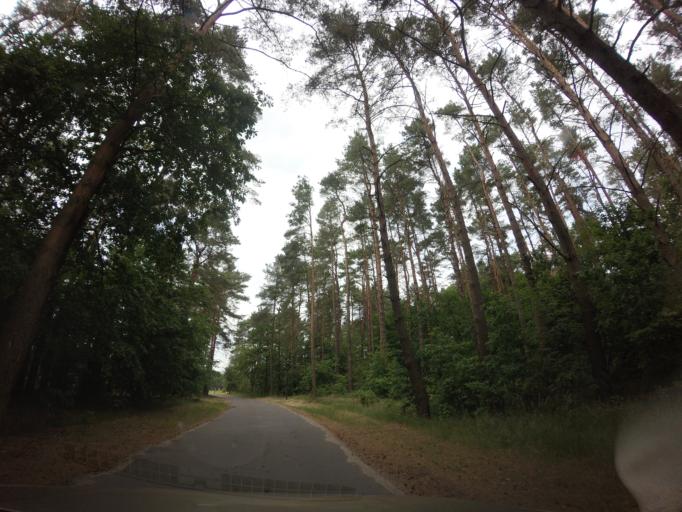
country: PL
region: West Pomeranian Voivodeship
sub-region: Powiat szczecinecki
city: Borne Sulinowo
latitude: 53.5892
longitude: 16.5298
